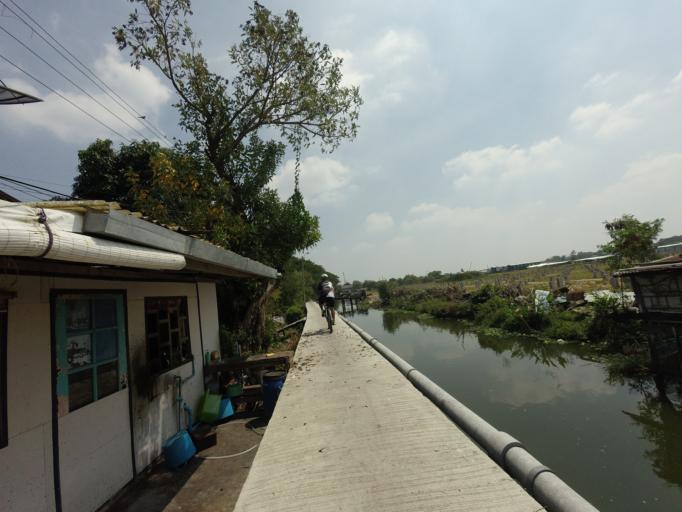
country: TH
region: Bangkok
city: Saphan Sung
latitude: 13.7546
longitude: 100.6729
